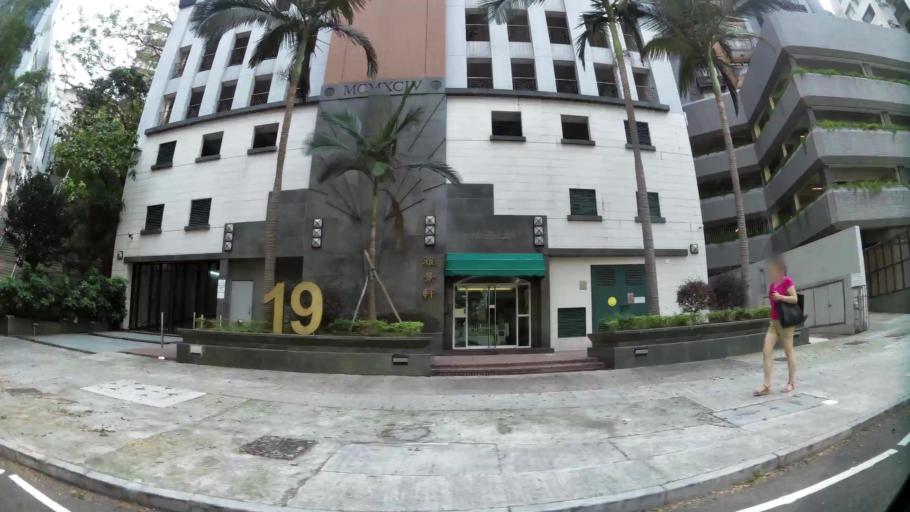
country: HK
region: Wanchai
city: Wan Chai
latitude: 22.2754
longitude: 114.1939
